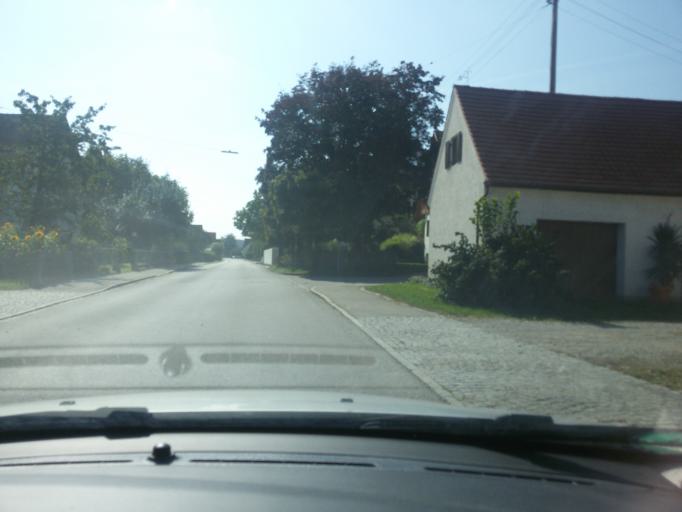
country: DE
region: Bavaria
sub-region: Swabia
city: Scherstetten
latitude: 48.1801
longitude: 10.6408
